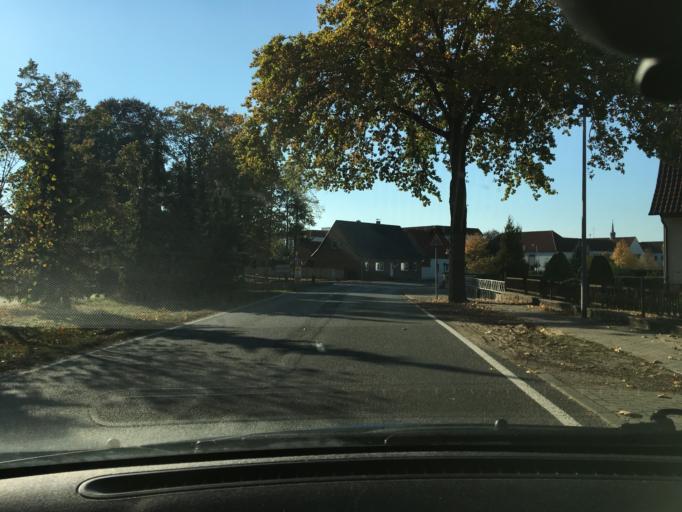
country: DE
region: Mecklenburg-Vorpommern
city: Domitz
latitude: 53.1348
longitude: 11.2714
